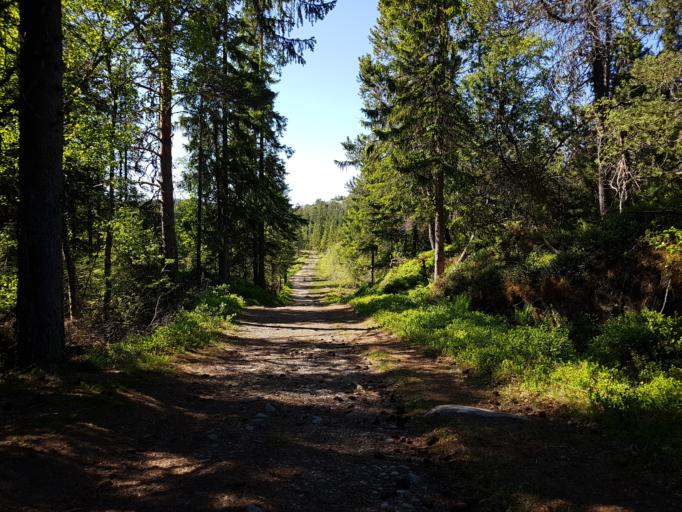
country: NO
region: Sor-Trondelag
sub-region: Trondheim
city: Trondheim
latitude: 63.4278
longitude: 10.2951
